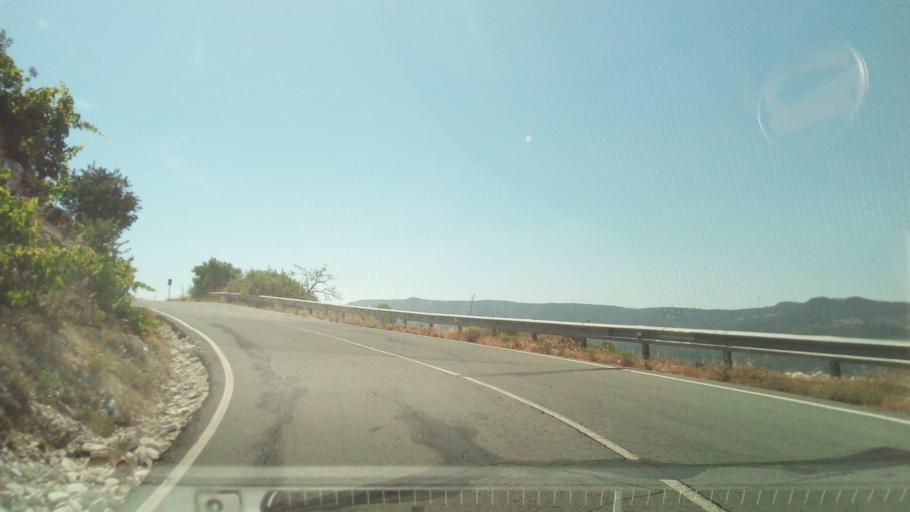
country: CY
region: Limassol
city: Pachna
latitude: 34.7981
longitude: 32.6883
